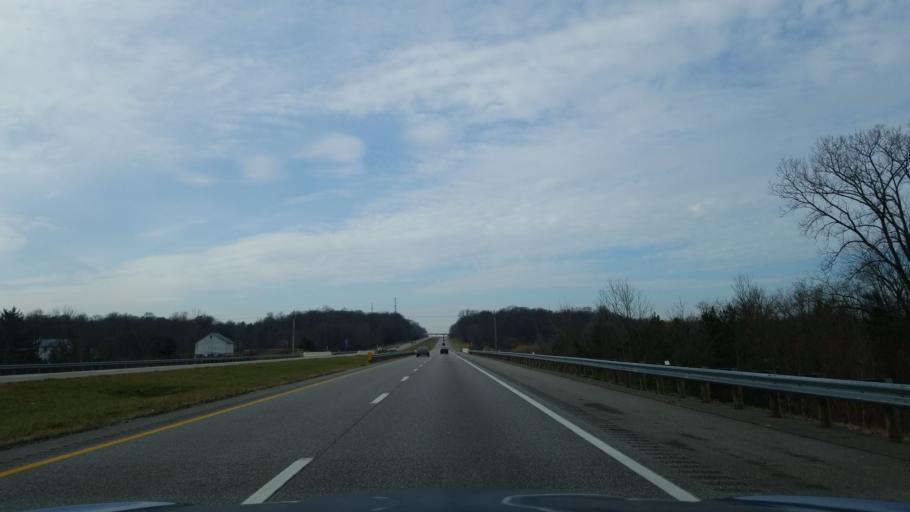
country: US
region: Ohio
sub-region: Geauga County
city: Bainbridge
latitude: 41.3839
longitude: -81.3059
